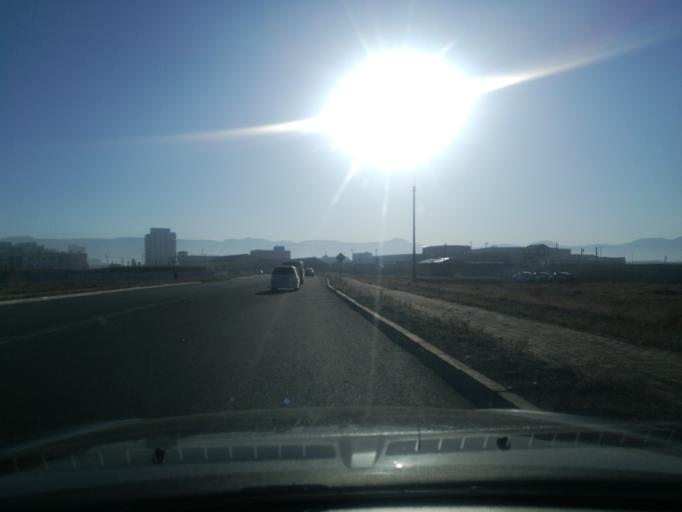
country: MN
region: Ulaanbaatar
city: Ulaanbaatar
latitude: 47.8566
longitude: 106.7532
